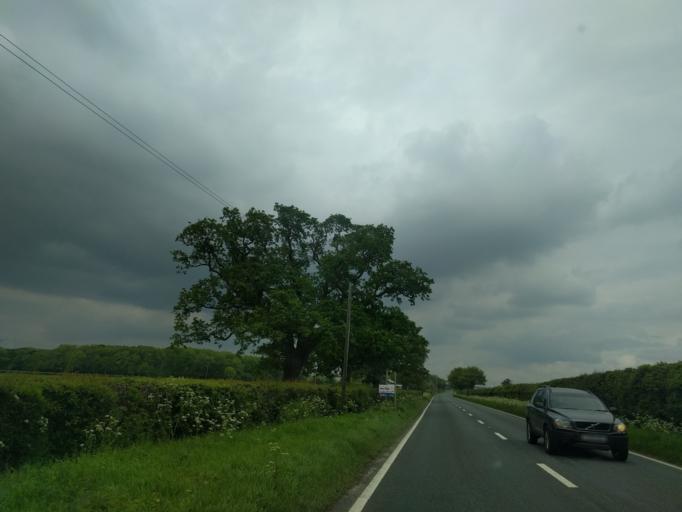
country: GB
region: England
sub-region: Somerset
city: Castle Cary
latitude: 51.0963
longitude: -2.6002
